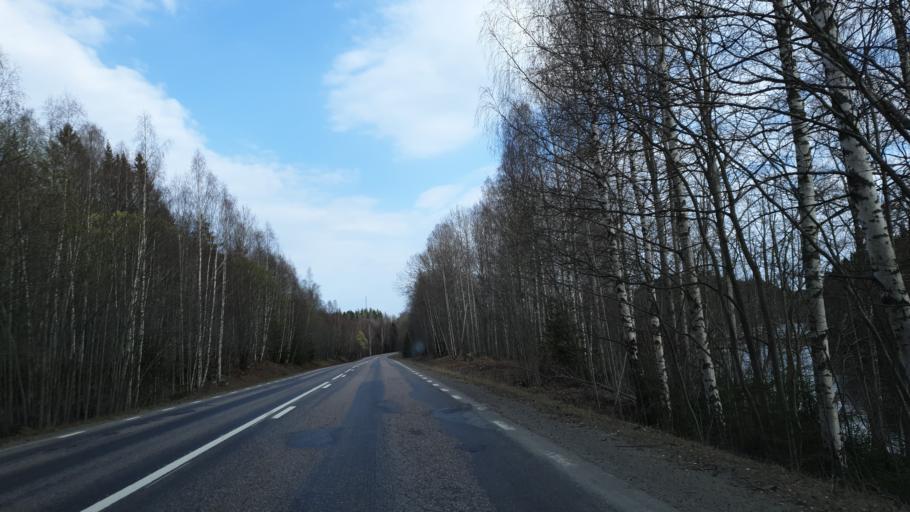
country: SE
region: Gaevleborg
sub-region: Hudiksvalls Kommun
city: Iggesund
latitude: 61.6497
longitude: 17.0390
